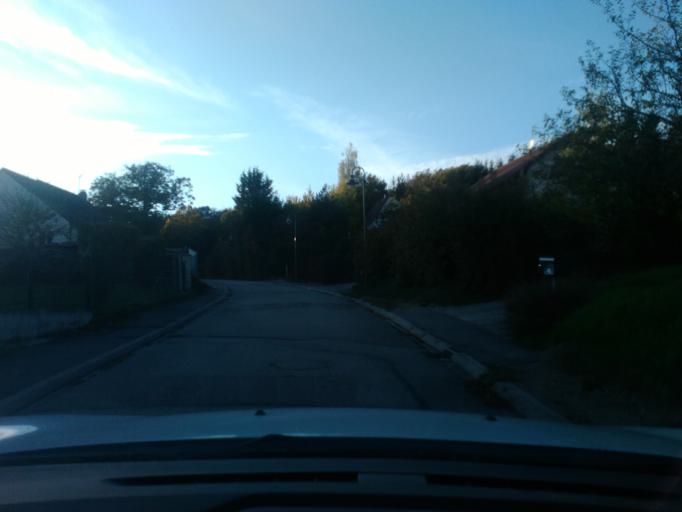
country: FR
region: Lorraine
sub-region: Departement des Vosges
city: Charmes
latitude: 48.3365
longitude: 6.2730
